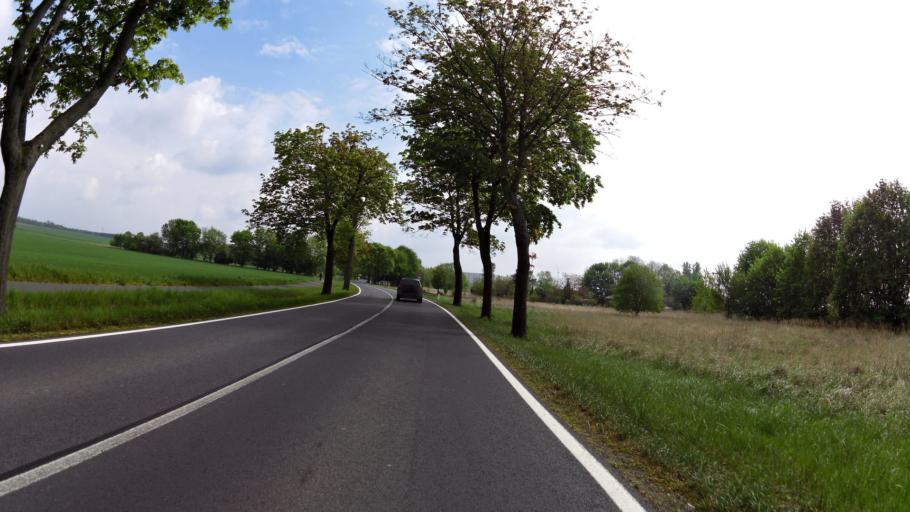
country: DE
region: Brandenburg
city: Mittenwalde
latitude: 52.2592
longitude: 13.5550
